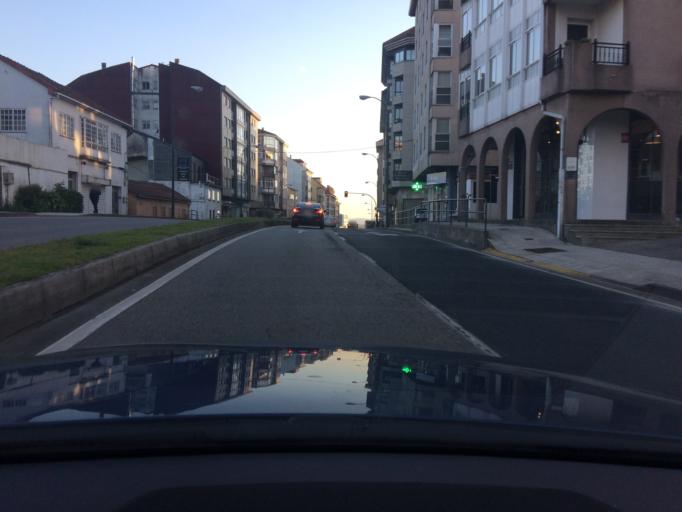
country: ES
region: Galicia
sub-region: Provincia da Coruna
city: Santiago de Compostela
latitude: 42.8430
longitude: -8.5779
